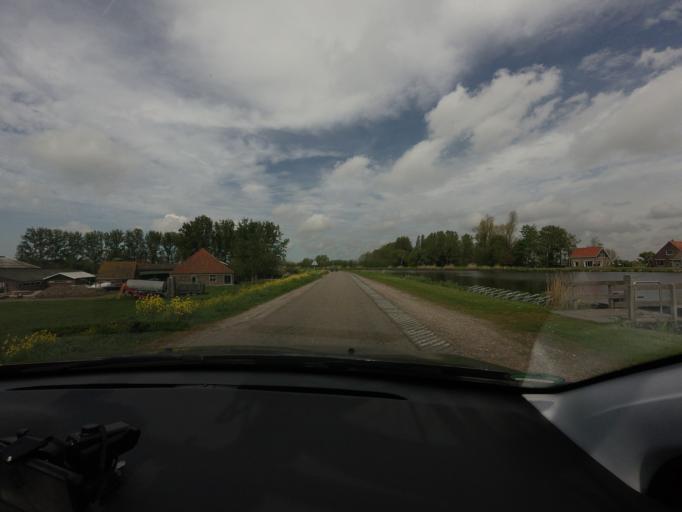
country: NL
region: North Holland
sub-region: Gemeente Uitgeest
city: Uitgeest
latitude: 52.5497
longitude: 4.8041
